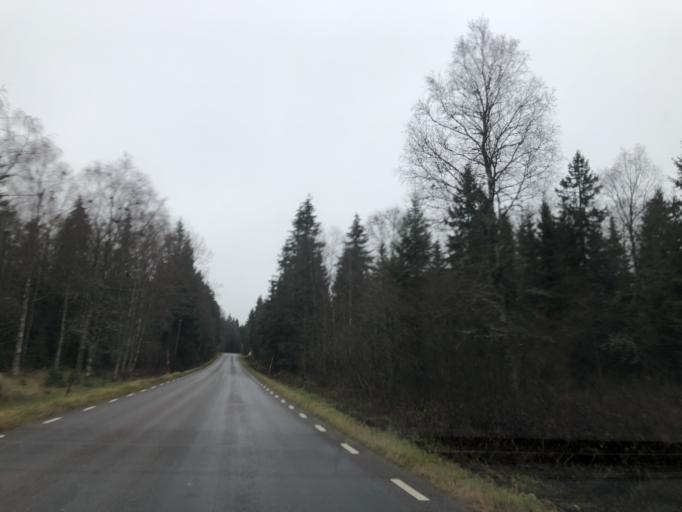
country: SE
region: Vaestra Goetaland
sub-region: Ulricehamns Kommun
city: Ulricehamn
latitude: 57.7615
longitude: 13.4824
